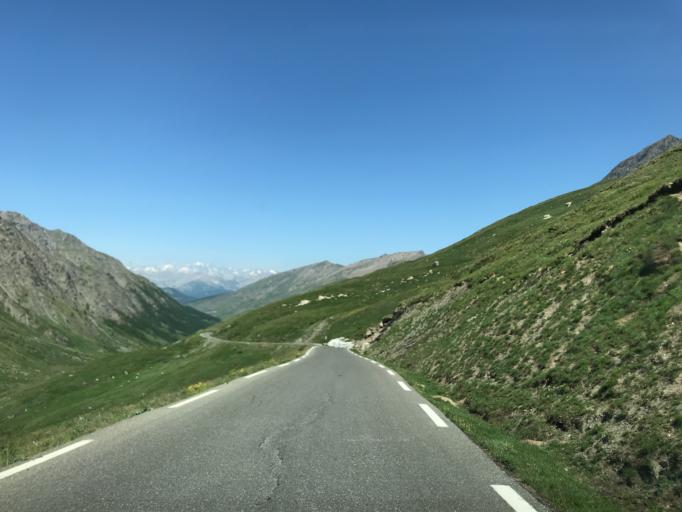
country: IT
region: Piedmont
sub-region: Provincia di Cuneo
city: Pontechianale
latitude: 44.6931
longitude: 6.9623
